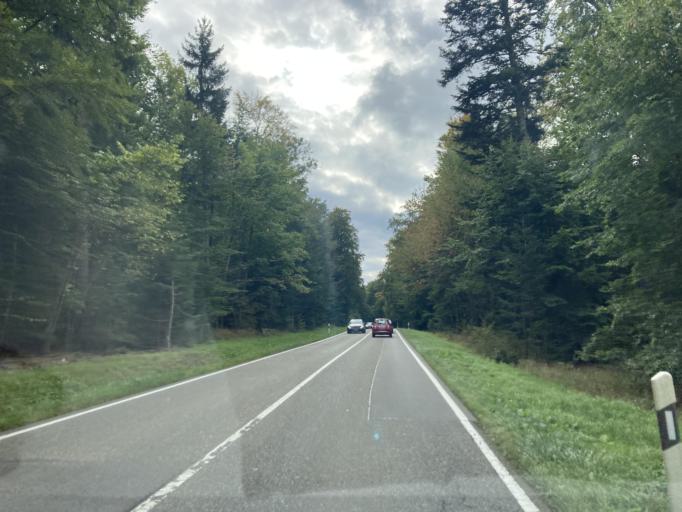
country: DE
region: Baden-Wuerttemberg
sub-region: Karlsruhe Region
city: Birkenfeld
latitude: 48.8623
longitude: 8.6130
